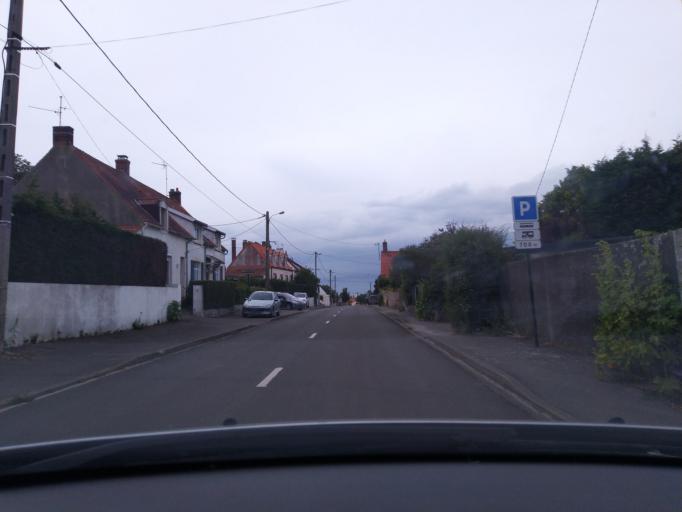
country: FR
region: Nord-Pas-de-Calais
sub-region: Departement du Pas-de-Calais
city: Wissant
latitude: 50.8828
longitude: 1.6655
